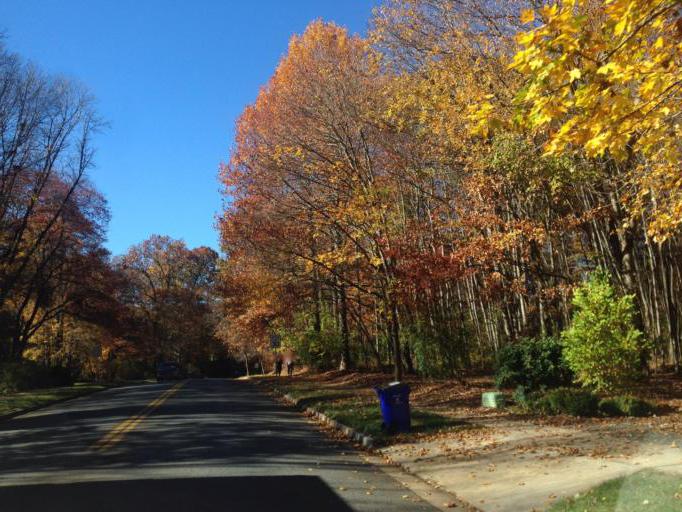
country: US
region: Maryland
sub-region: Howard County
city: Riverside
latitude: 39.1932
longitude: -76.8744
